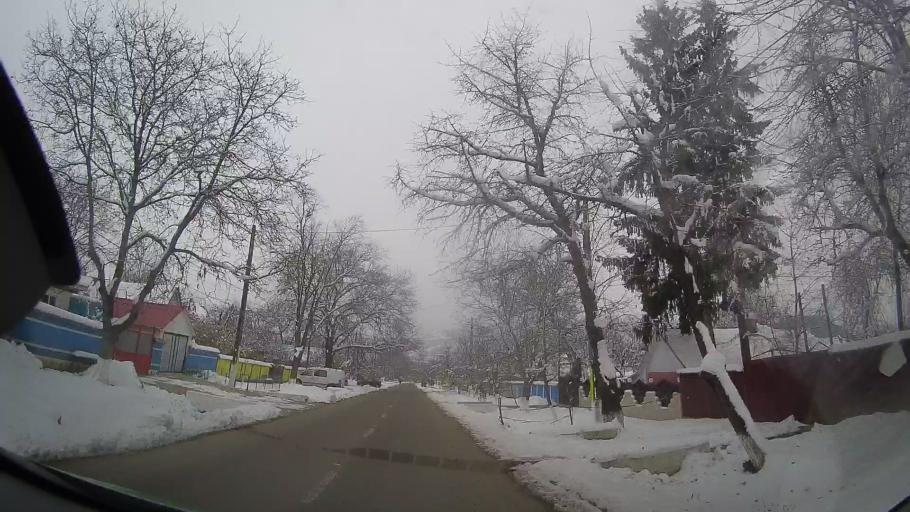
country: RO
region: Vaslui
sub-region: Comuna Bacesti
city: Bacesti
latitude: 46.8192
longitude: 27.2039
